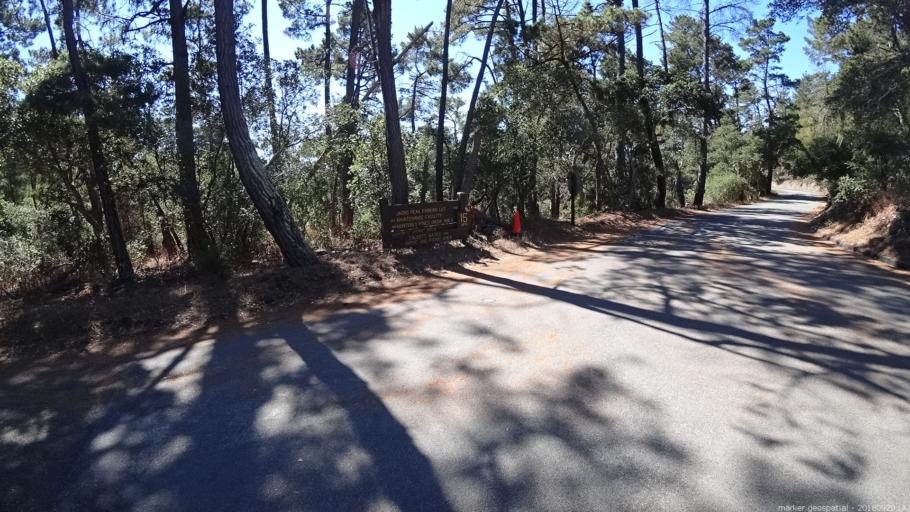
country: US
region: California
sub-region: Monterey County
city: Del Rey Oaks
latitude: 36.5651
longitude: -121.8634
